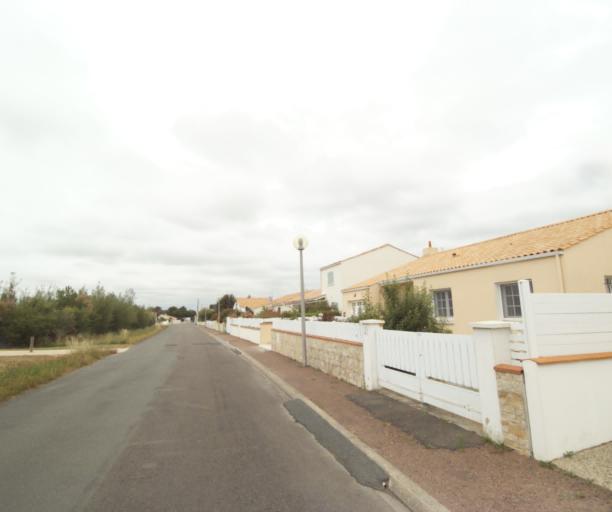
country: FR
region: Pays de la Loire
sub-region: Departement de la Vendee
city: Chateau-d'Olonne
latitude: 46.4981
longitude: -1.7514
